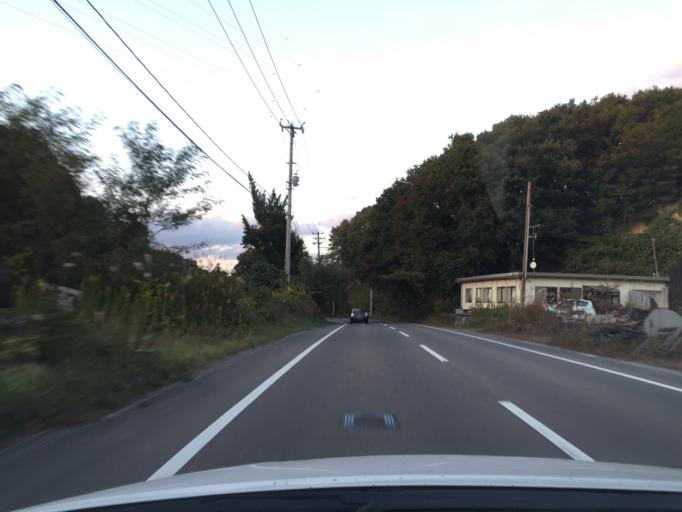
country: JP
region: Fukushima
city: Miharu
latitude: 37.3920
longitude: 140.4424
